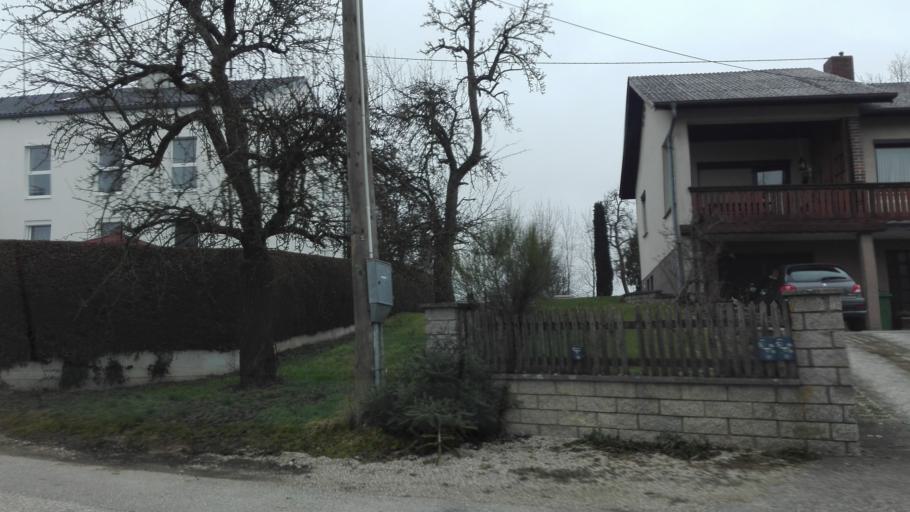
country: AT
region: Upper Austria
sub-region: Wels-Land
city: Holzhausen
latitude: 48.2361
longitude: 14.1337
